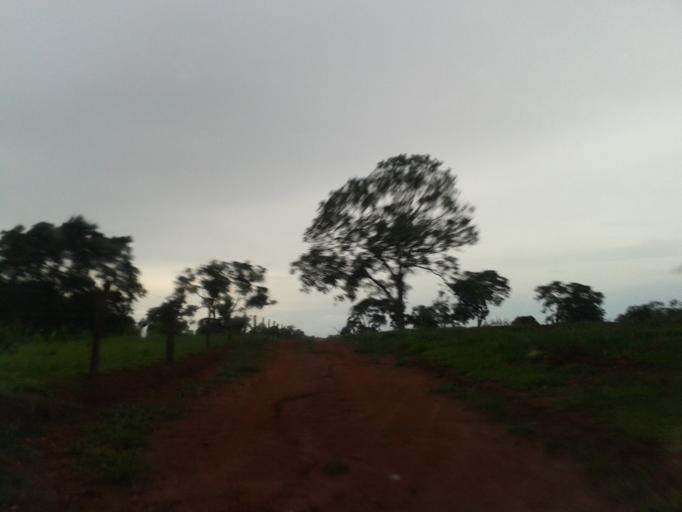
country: BR
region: Minas Gerais
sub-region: Santa Vitoria
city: Santa Vitoria
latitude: -19.2286
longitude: -50.5035
